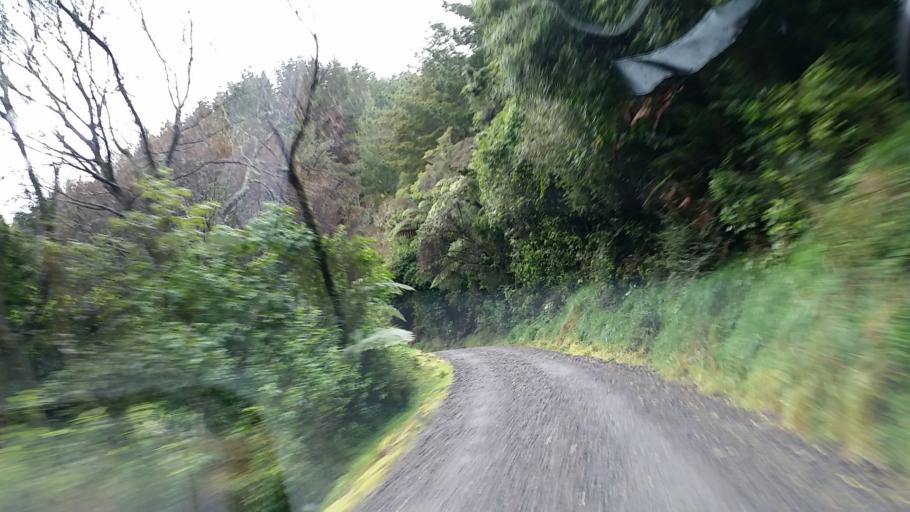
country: NZ
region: Taranaki
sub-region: South Taranaki District
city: Eltham
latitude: -39.5034
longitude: 174.4315
